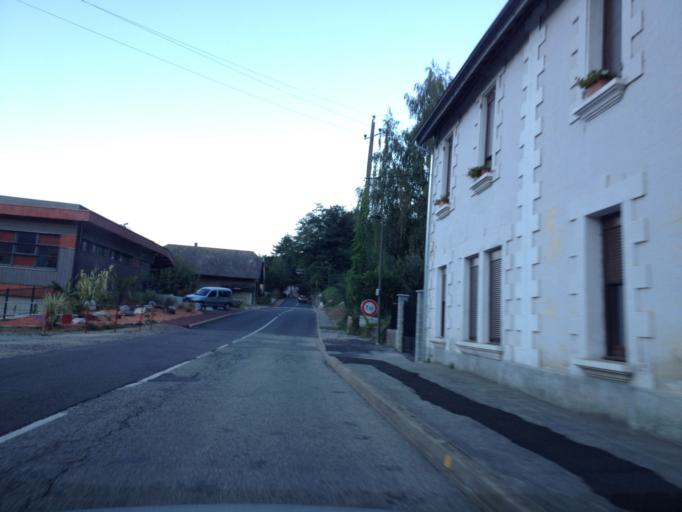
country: FR
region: Rhone-Alpes
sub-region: Departement de la Savoie
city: Voglans
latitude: 45.6271
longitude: 5.8936
